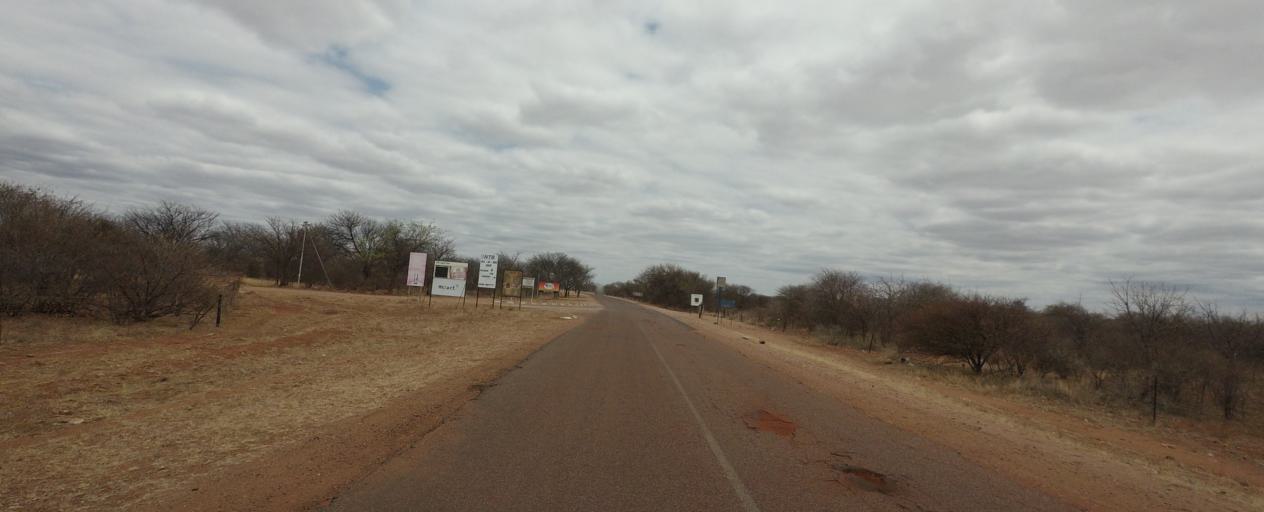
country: BW
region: Central
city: Makobeng
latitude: -22.8471
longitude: 28.2046
